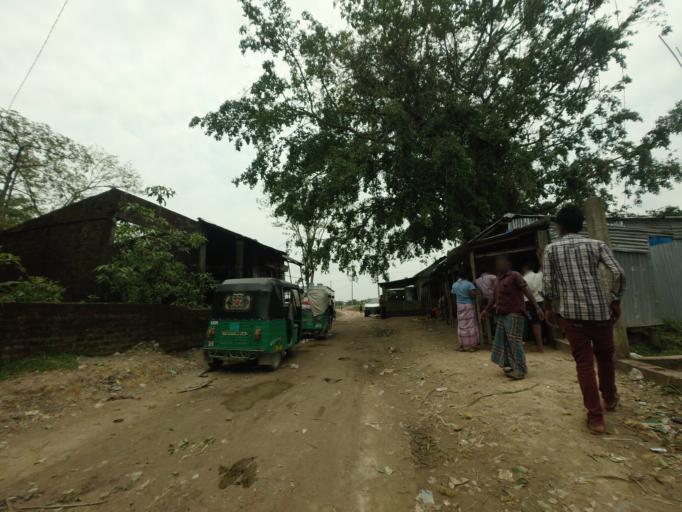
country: BD
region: Sylhet
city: Sylhet
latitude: 25.0063
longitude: 91.9165
